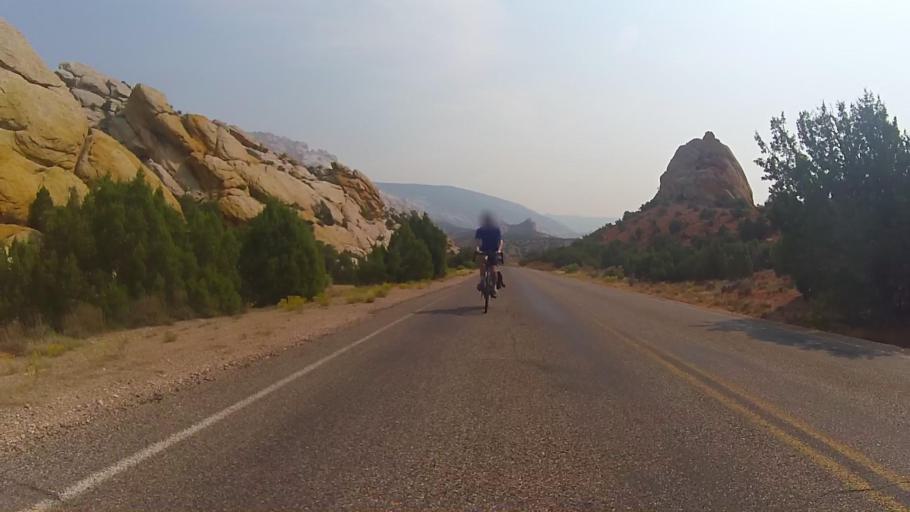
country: US
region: Utah
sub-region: Uintah County
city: Naples
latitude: 40.4419
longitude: -109.2582
